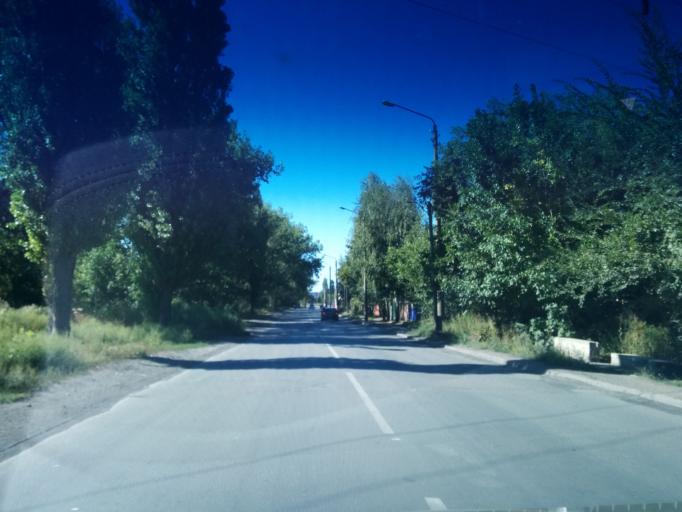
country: RU
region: Rostov
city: Shakhty
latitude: 47.6813
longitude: 40.2791
